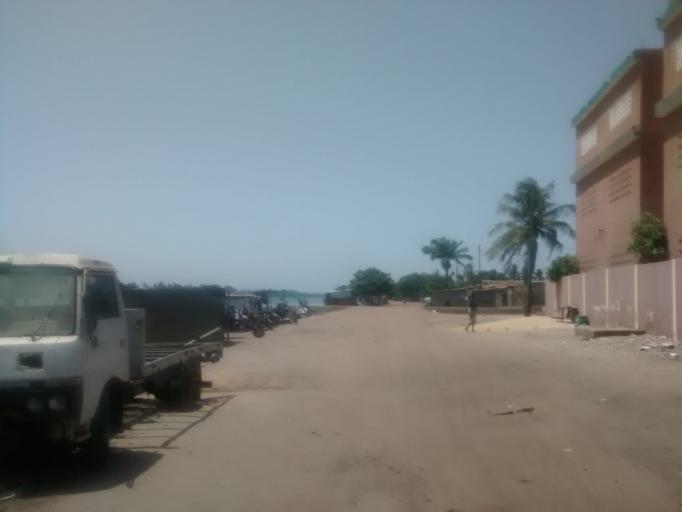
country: TG
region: Maritime
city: Lome
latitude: 6.1454
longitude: 1.2350
